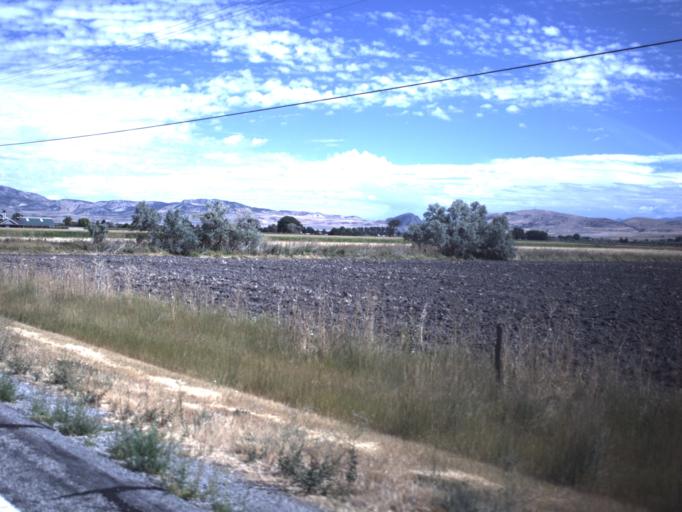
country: US
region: Utah
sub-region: Box Elder County
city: Garland
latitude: 41.7547
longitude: -112.1483
